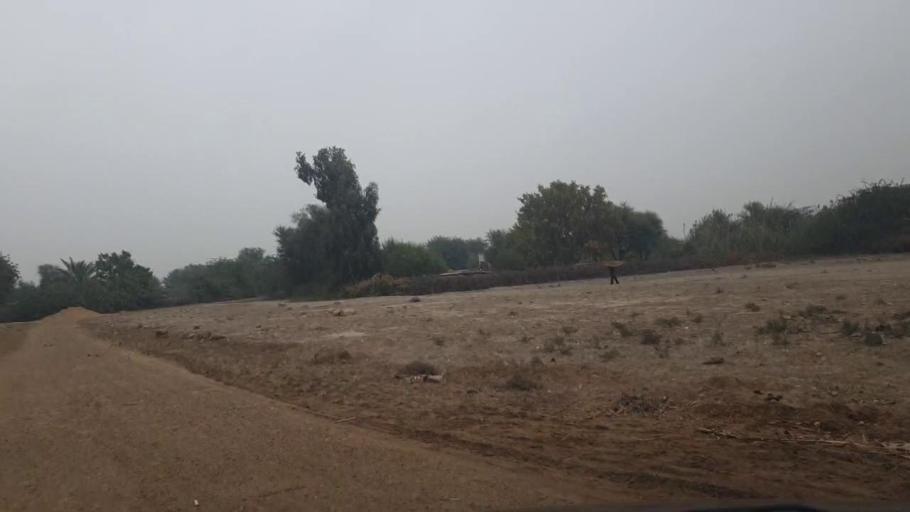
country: PK
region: Sindh
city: Tando Adam
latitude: 25.7900
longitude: 68.6676
